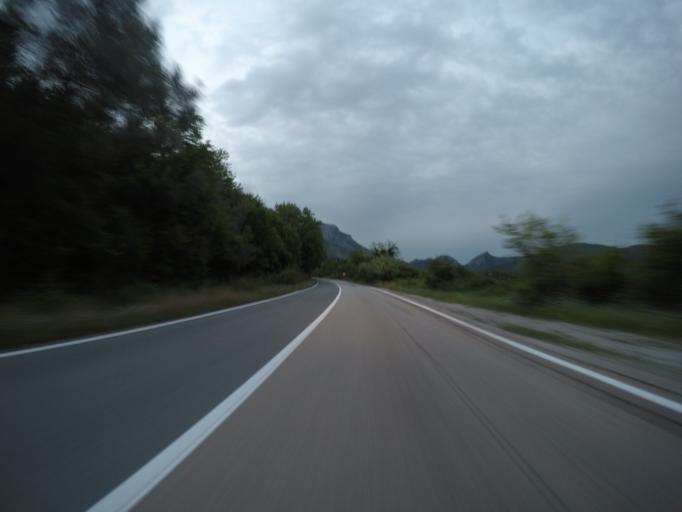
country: ME
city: Petrovac na Moru
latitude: 42.1979
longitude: 18.9692
